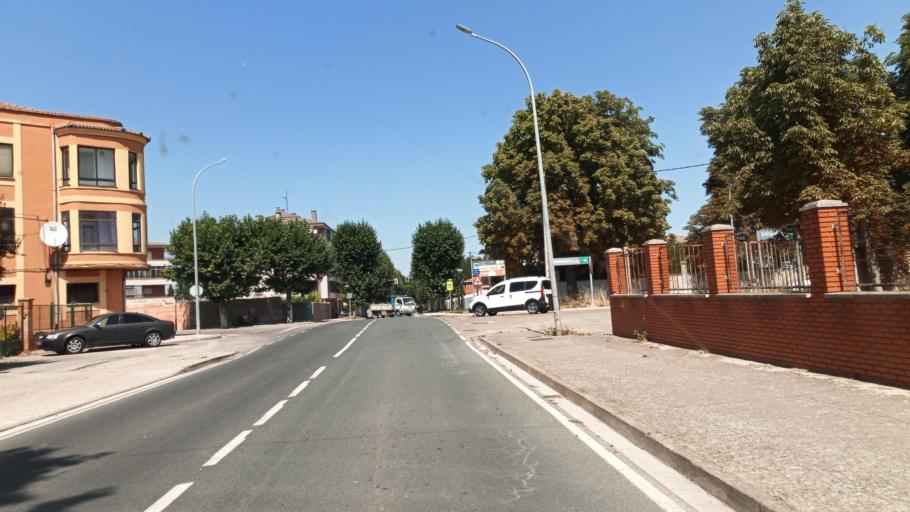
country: ES
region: Castille and Leon
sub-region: Provincia de Burgos
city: Briviesca
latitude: 42.5424
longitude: -3.3203
